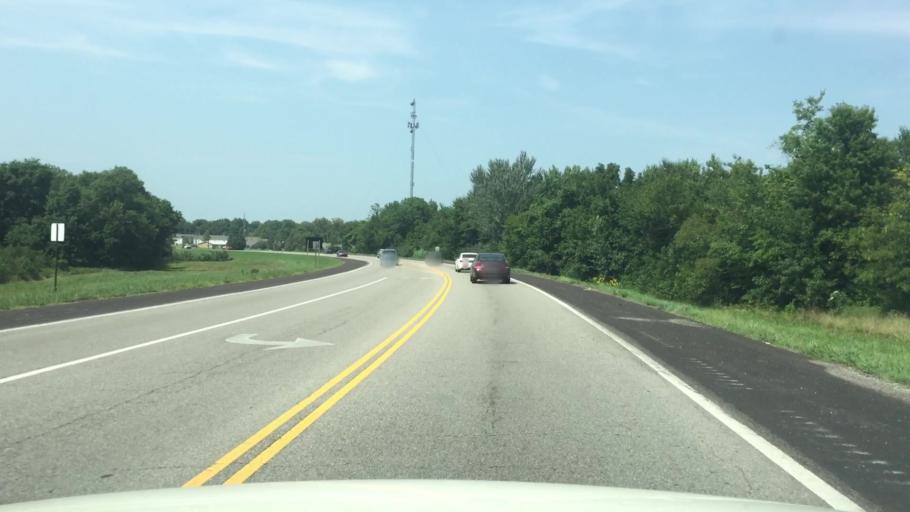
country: US
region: Kansas
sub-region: Crawford County
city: Pittsburg
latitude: 37.3830
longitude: -94.7072
